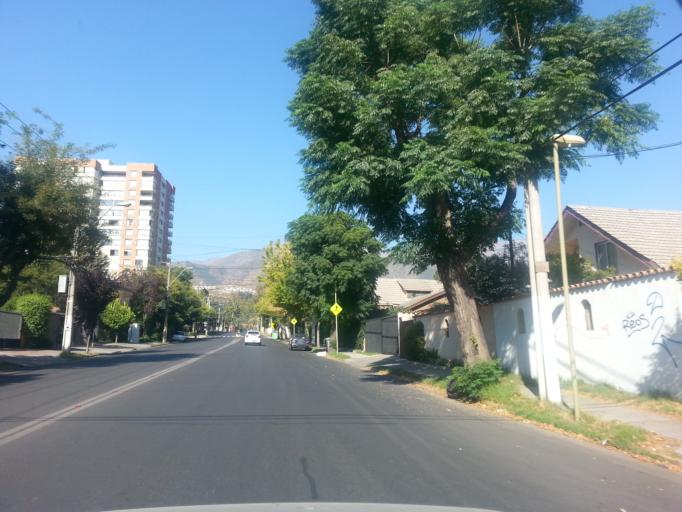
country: CL
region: Santiago Metropolitan
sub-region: Provincia de Santiago
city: Villa Presidente Frei, Nunoa, Santiago, Chile
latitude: -33.4242
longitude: -70.5416
